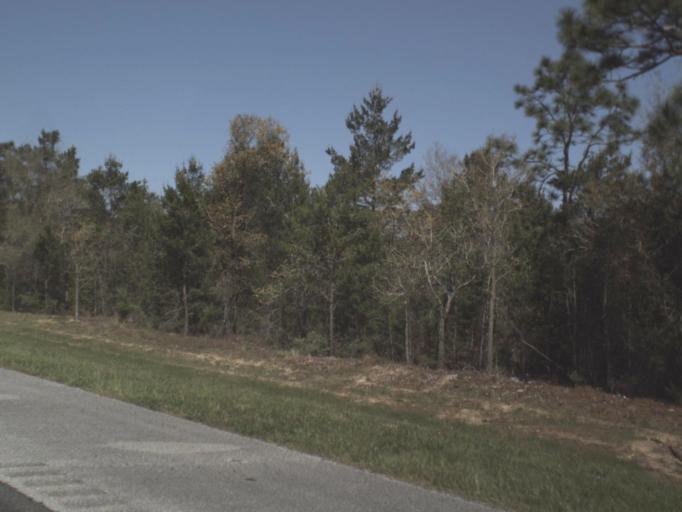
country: US
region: Florida
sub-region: Okaloosa County
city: Crestview
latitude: 30.7341
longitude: -86.3702
